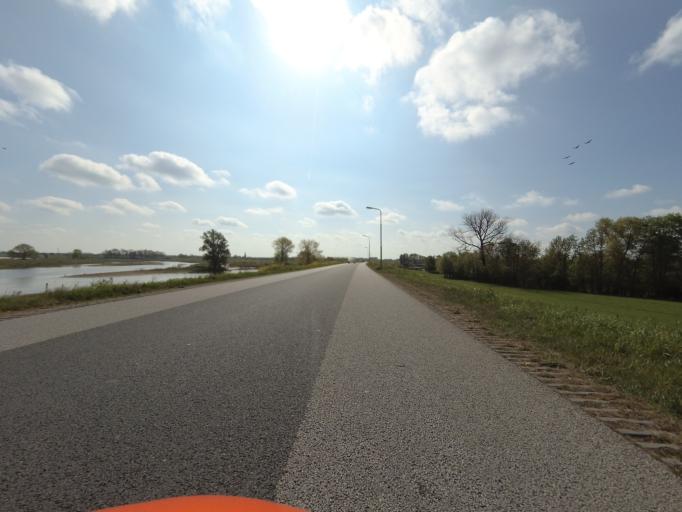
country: NL
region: Utrecht
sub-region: Gemeente IJsselstein
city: IJsselstein
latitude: 51.9673
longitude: 5.0188
